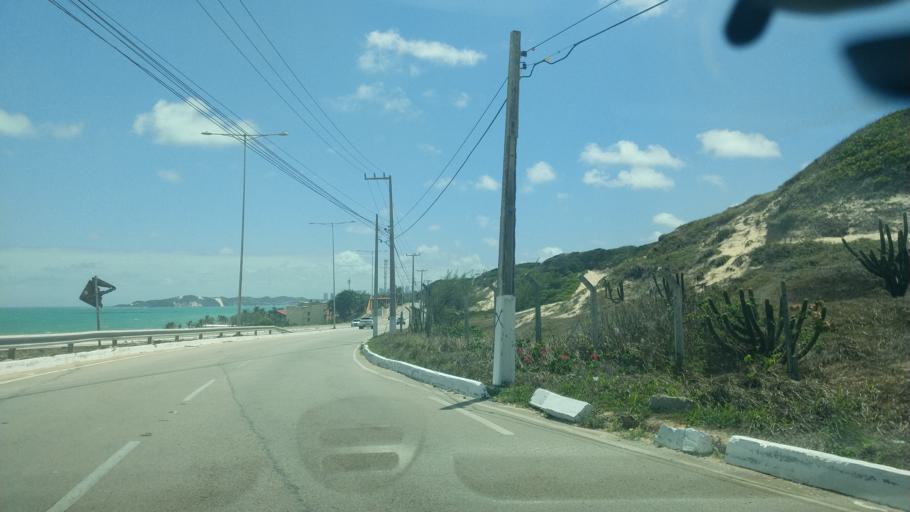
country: BR
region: Rio Grande do Norte
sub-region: Natal
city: Natal
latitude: -5.8234
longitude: -35.1833
